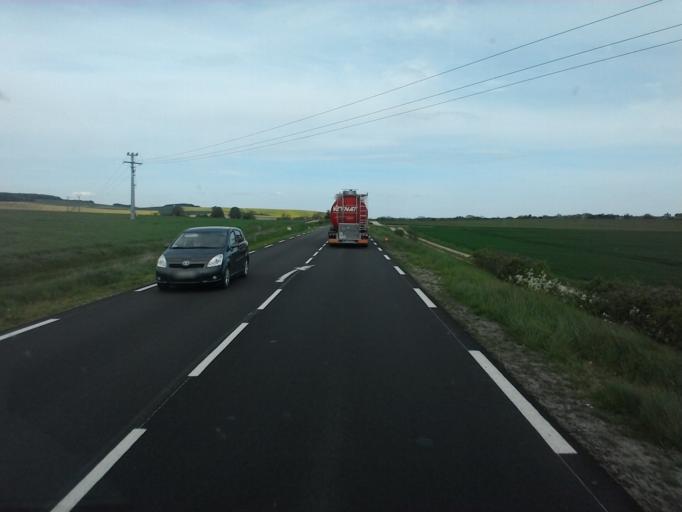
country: FR
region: Champagne-Ardenne
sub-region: Departement de l'Aube
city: Bouilly
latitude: 48.1217
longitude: 3.9510
